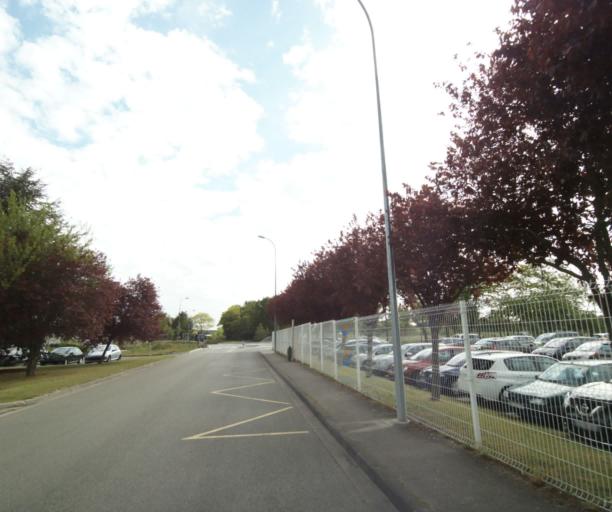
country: FR
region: Ile-de-France
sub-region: Departement des Yvelines
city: Bouafle
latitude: 48.9801
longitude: 1.8942
